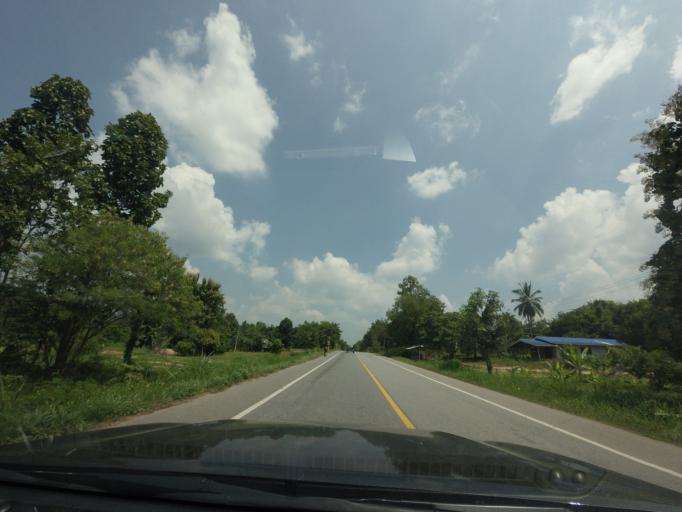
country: TH
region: Phitsanulok
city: Chat Trakan
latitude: 17.2990
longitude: 100.4191
